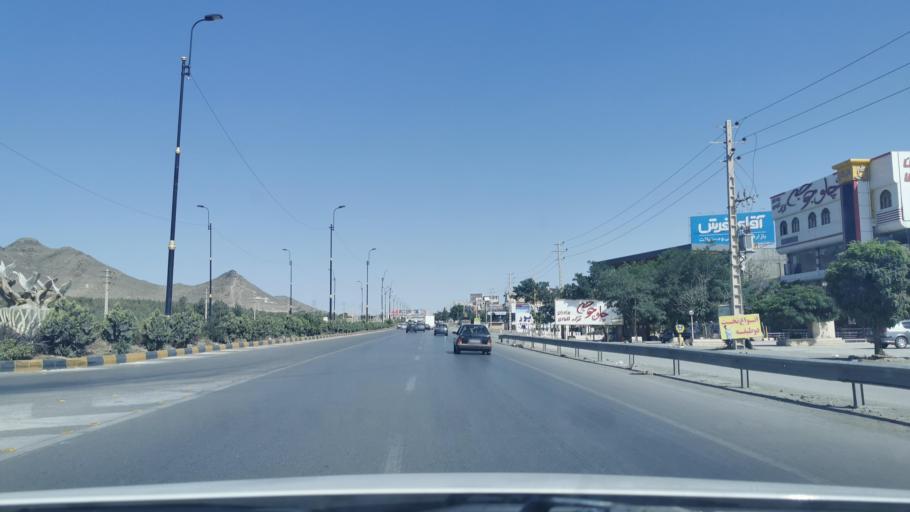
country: IR
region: Razavi Khorasan
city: Torqabeh
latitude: 36.3896
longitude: 59.4068
